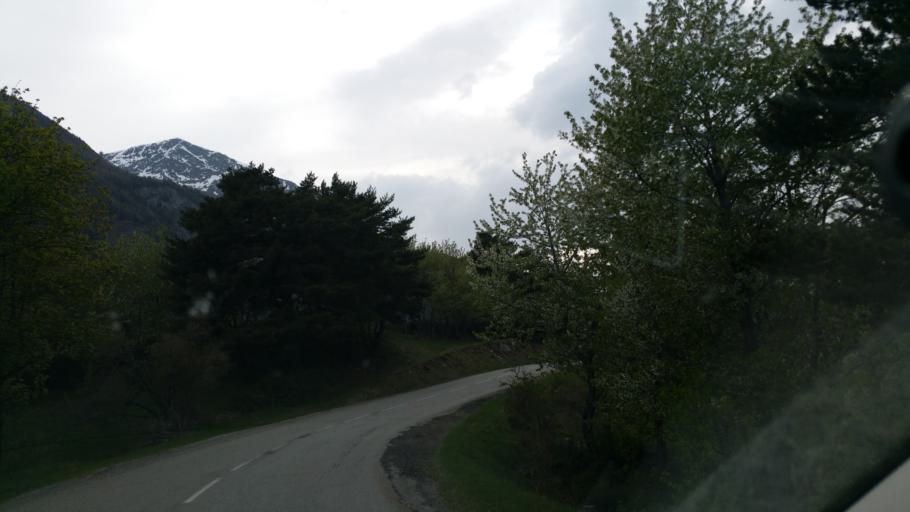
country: FR
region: Rhone-Alpes
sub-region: Departement de la Savoie
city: Modane
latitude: 45.2025
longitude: 6.6132
